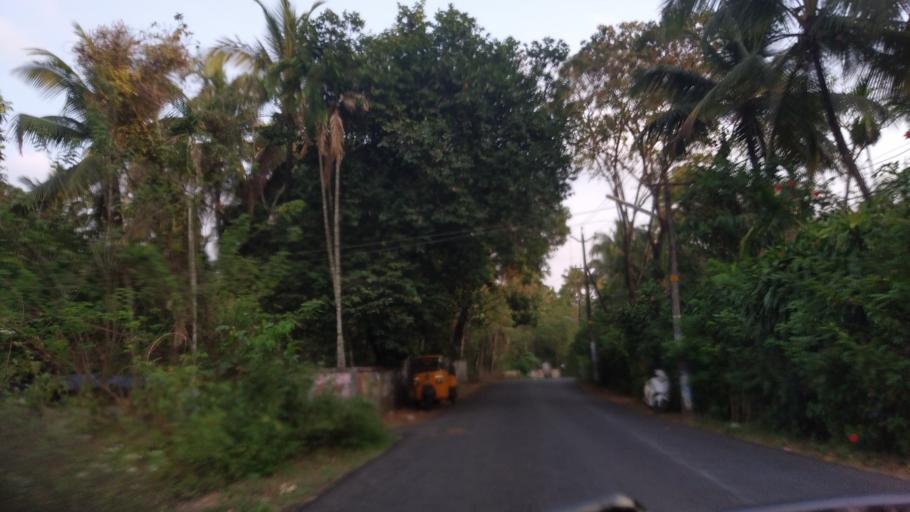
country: IN
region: Kerala
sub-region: Thrissur District
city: Thanniyam
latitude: 10.3599
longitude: 76.1090
